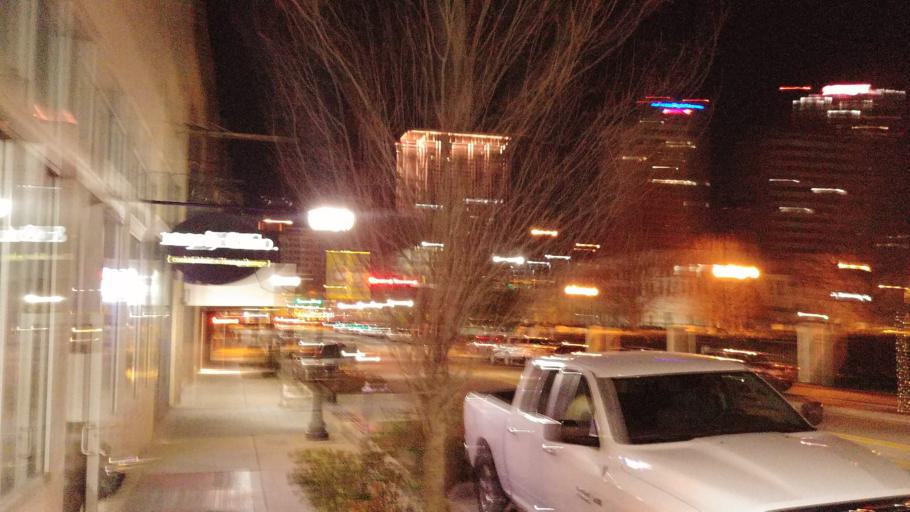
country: US
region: Arkansas
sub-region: Pulaski County
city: Little Rock
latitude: 34.7478
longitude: -92.2703
